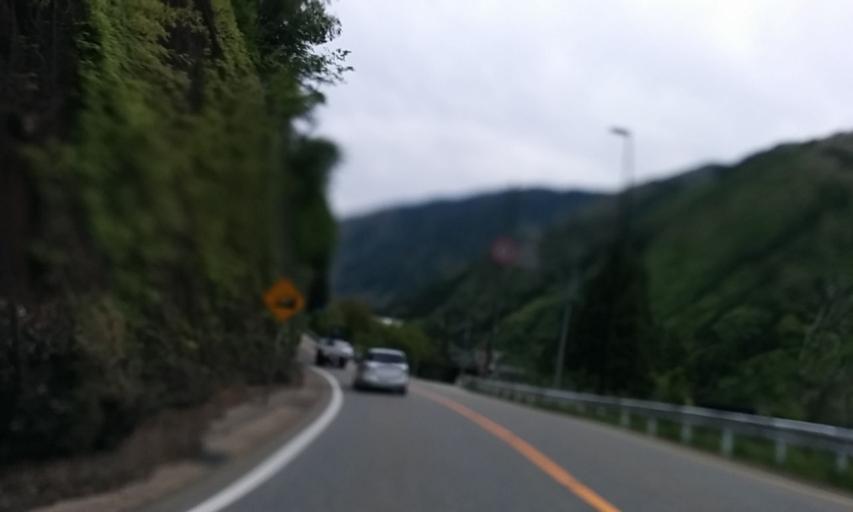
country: JP
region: Gifu
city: Takayama
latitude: 35.9938
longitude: 137.2790
